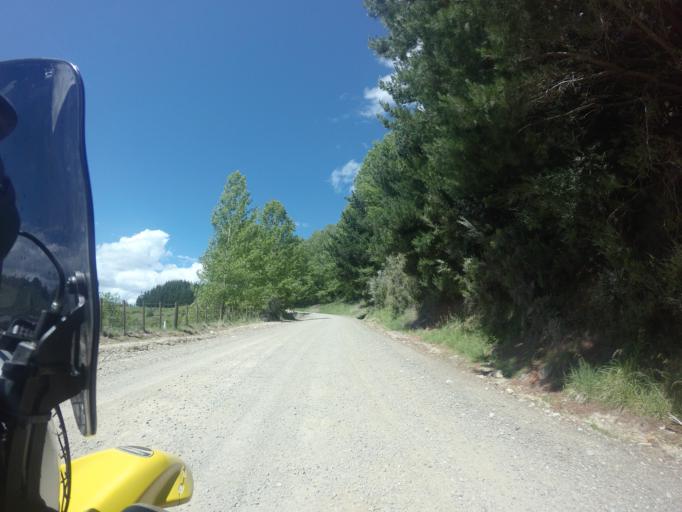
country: NZ
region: Hawke's Bay
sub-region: Wairoa District
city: Wairoa
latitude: -38.9888
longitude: 177.7207
